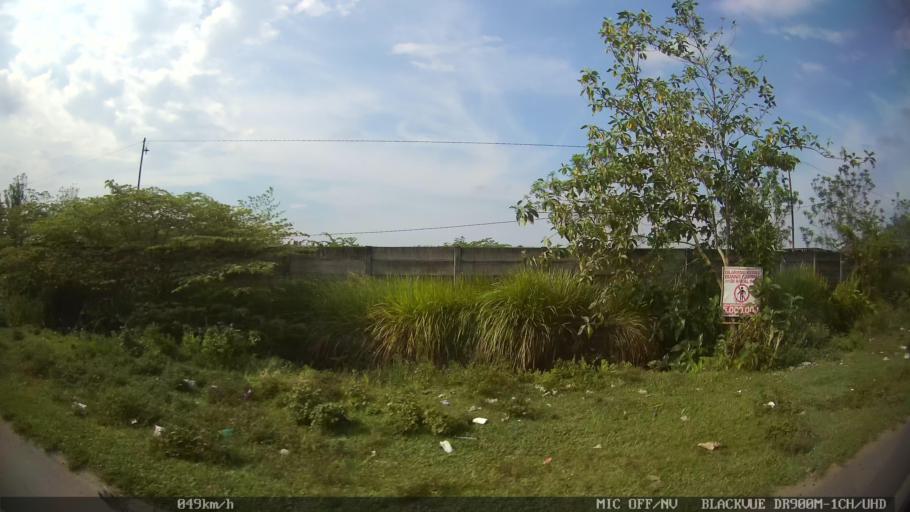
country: ID
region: North Sumatra
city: Medan
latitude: 3.5731
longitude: 98.7608
